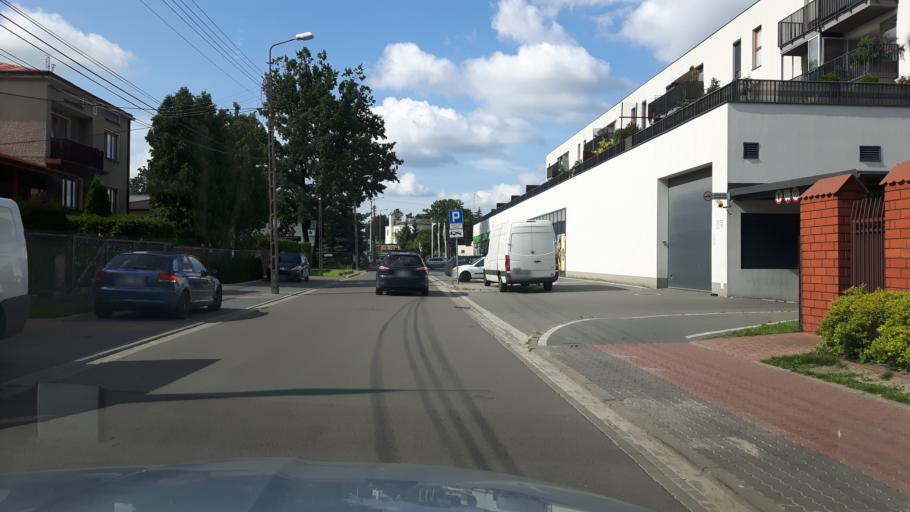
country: PL
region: Masovian Voivodeship
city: Zielonka
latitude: 52.3006
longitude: 21.1578
